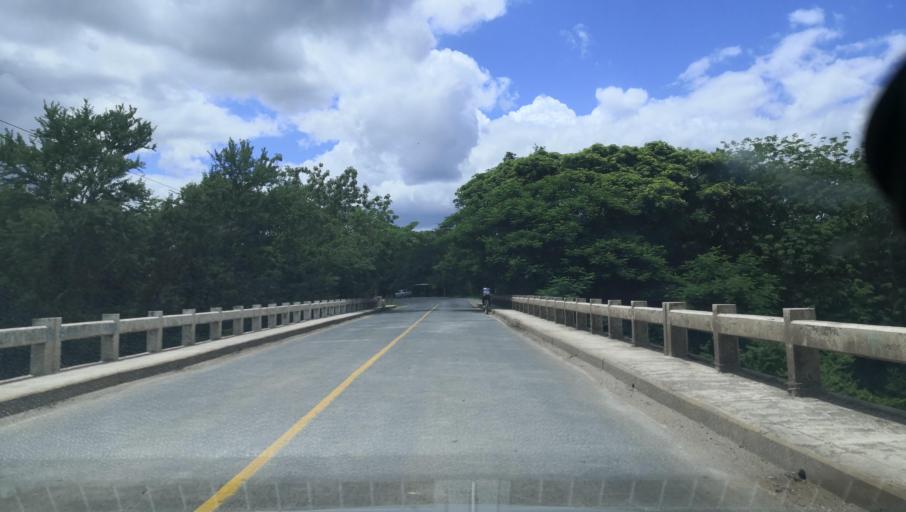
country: NI
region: Madriz
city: Palacaguina
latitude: 13.4154
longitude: -86.3978
